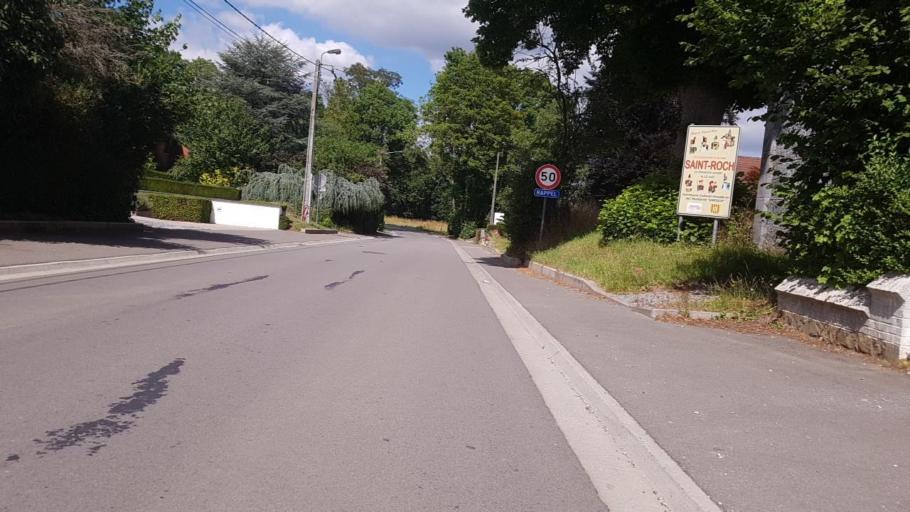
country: BE
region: Wallonia
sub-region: Province de Namur
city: Walcourt
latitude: 50.3265
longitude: 4.3796
